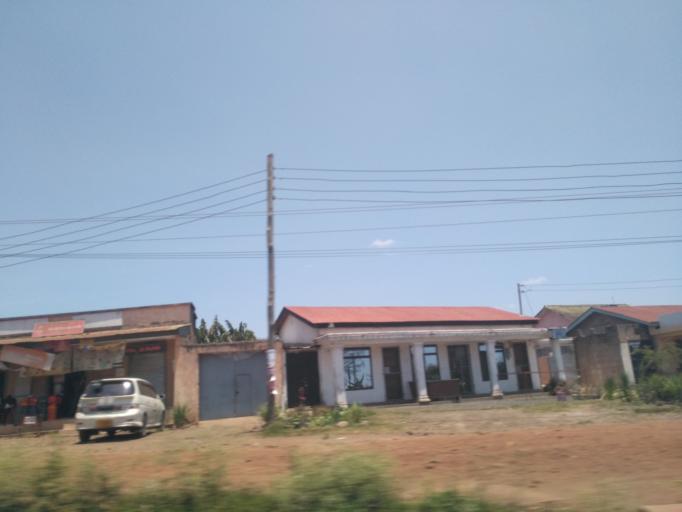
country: TZ
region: Arusha
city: Arusha
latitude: -3.3701
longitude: 36.6754
